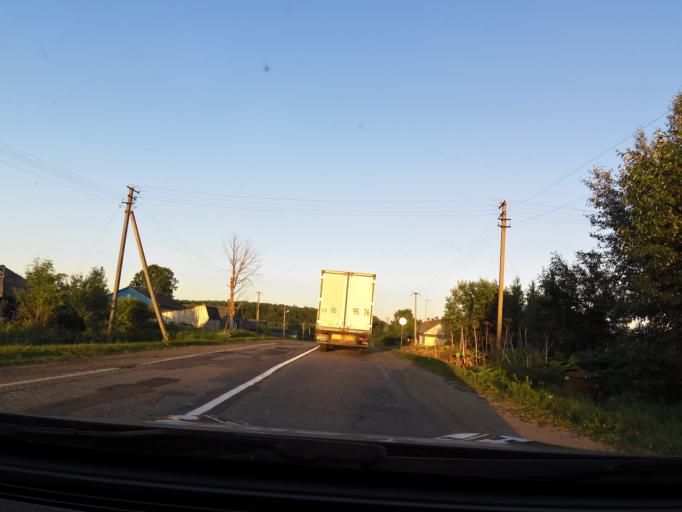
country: RU
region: Jaroslavl
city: Prechistoye
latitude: 58.4069
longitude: 40.3740
